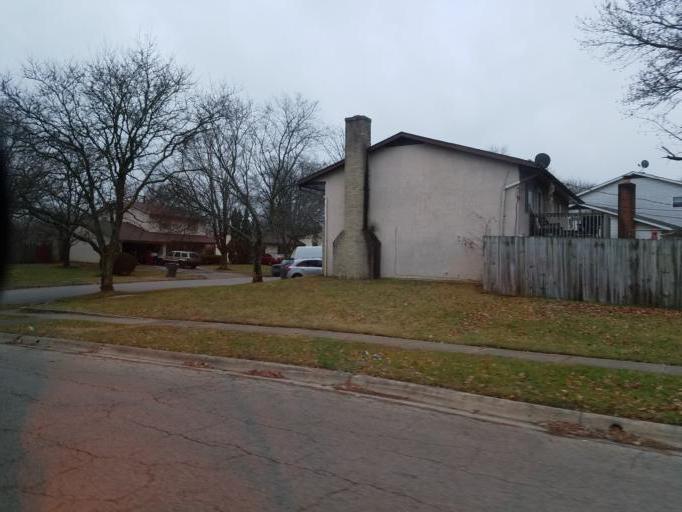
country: US
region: Ohio
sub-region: Franklin County
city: Minerva Park
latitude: 40.0825
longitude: -82.9698
